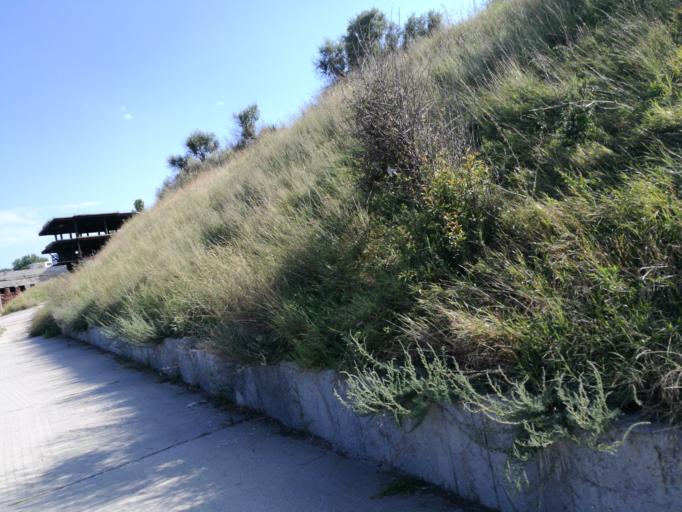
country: RO
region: Constanta
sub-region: Oras Eforie
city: Eforie
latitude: 44.0403
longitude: 28.6490
